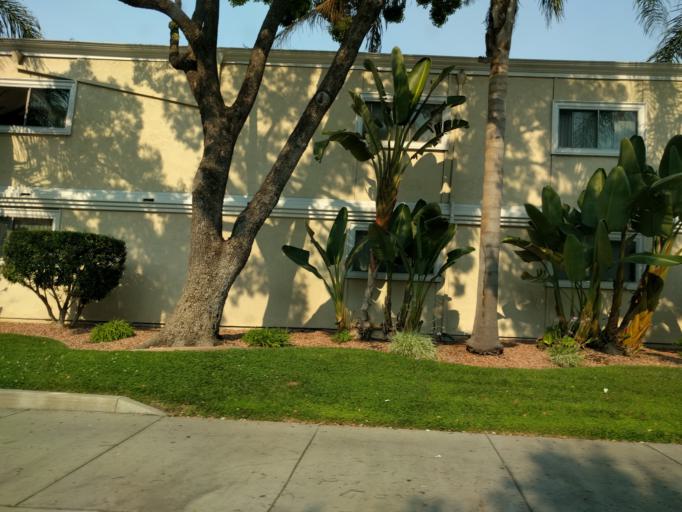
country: US
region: California
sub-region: Santa Clara County
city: Alum Rock
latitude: 37.3690
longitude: -121.8418
